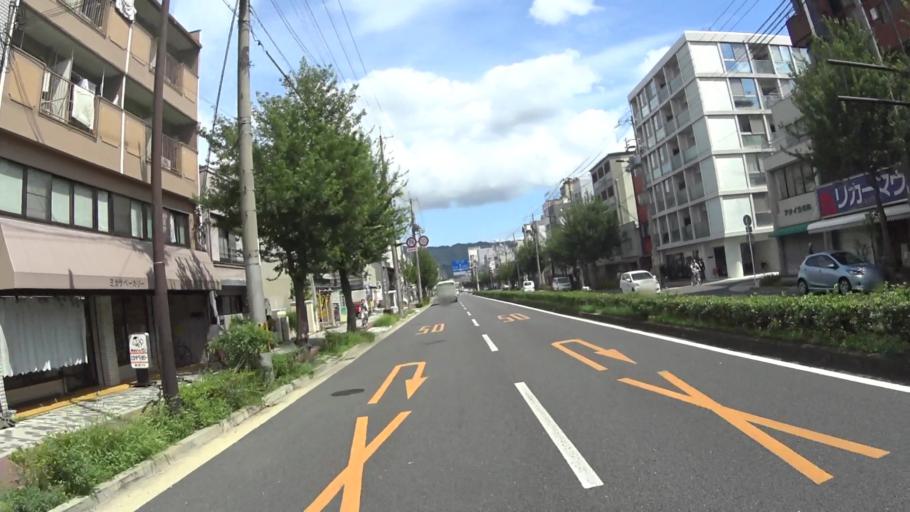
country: JP
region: Kyoto
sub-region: Kyoto-shi
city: Kamigyo-ku
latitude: 35.0442
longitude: 135.7676
